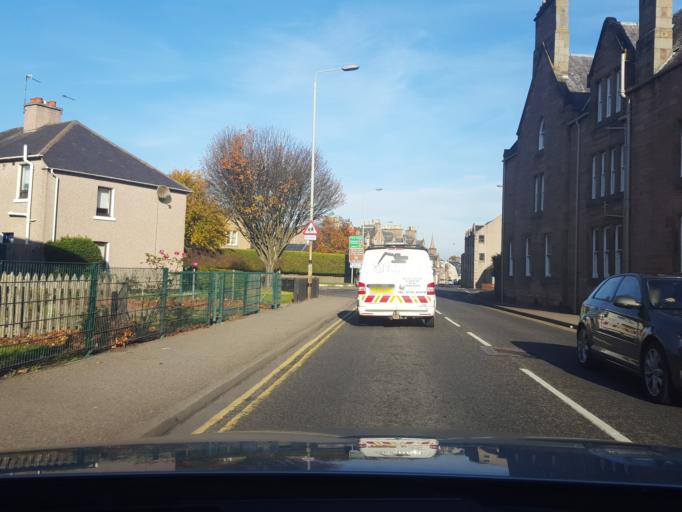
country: GB
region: Scotland
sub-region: Highland
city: Inverness
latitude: 57.4739
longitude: -4.2339
